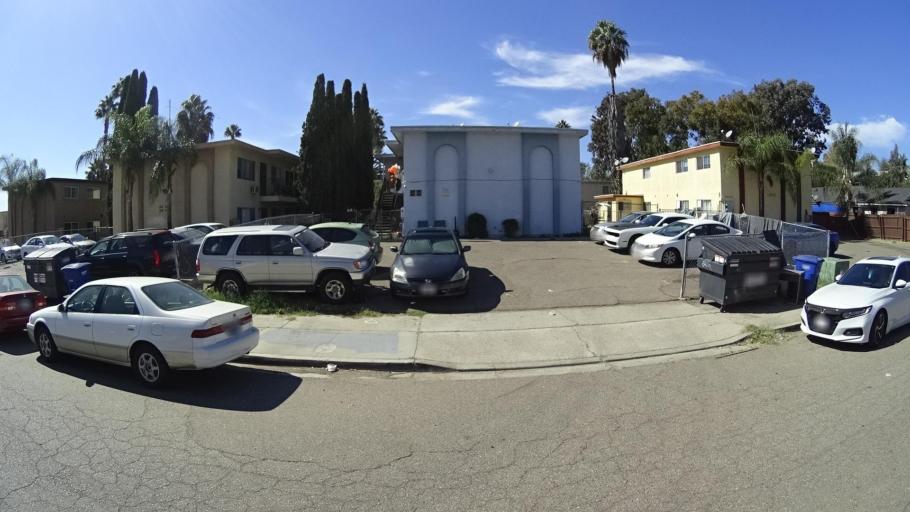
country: US
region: California
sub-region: San Diego County
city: La Presa
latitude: 32.7154
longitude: -117.0080
